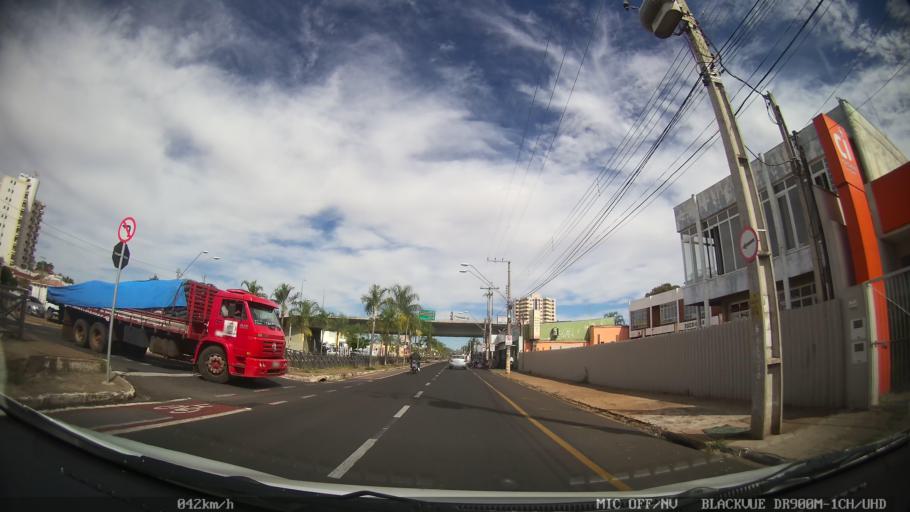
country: BR
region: Sao Paulo
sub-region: Catanduva
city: Catanduva
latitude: -21.1407
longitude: -48.9686
